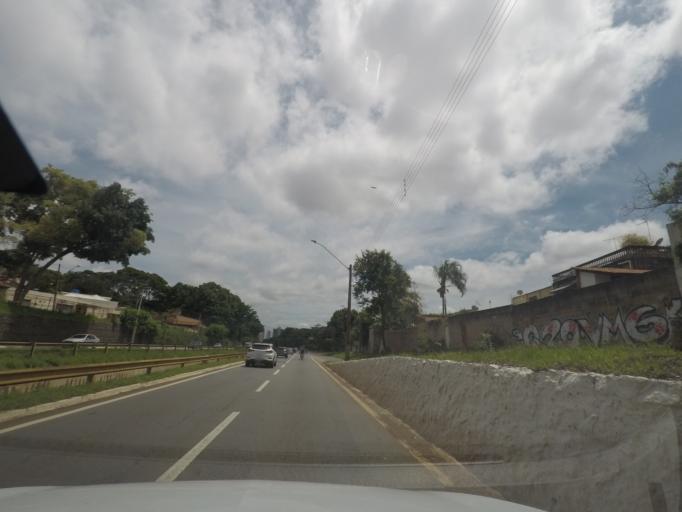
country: BR
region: Goias
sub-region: Goiania
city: Goiania
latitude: -16.6710
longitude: -49.2503
